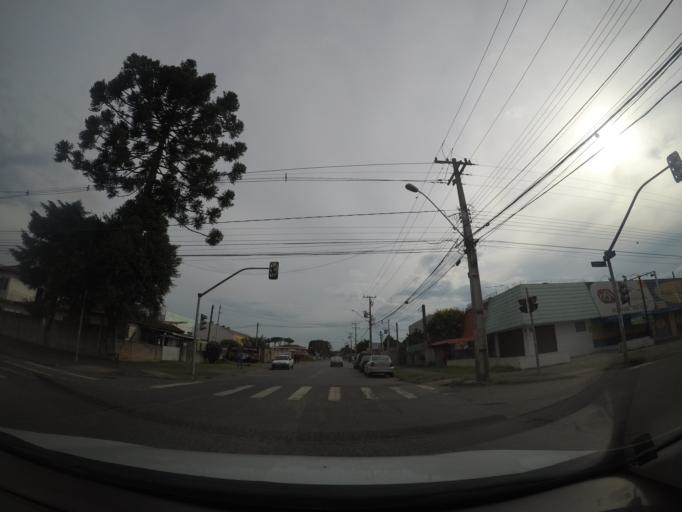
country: BR
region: Parana
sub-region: Sao Jose Dos Pinhais
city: Sao Jose dos Pinhais
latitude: -25.5030
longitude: -49.2257
